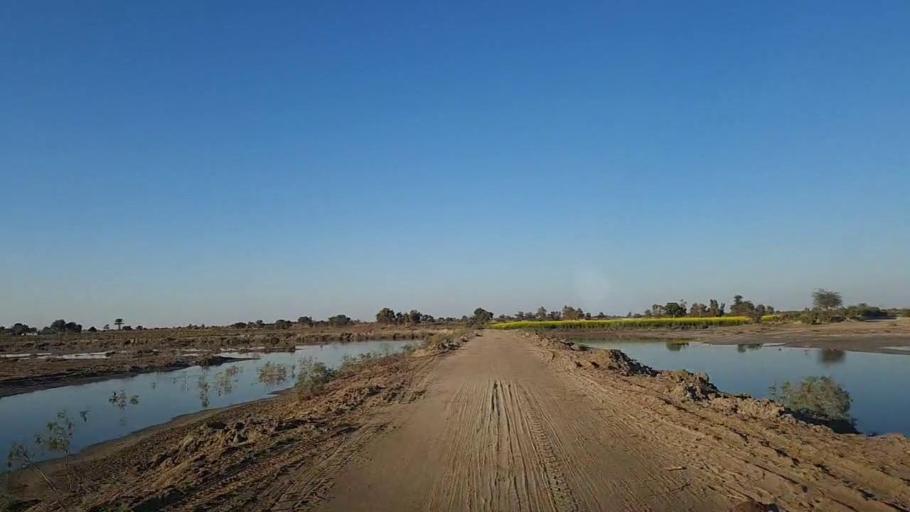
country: PK
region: Sindh
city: Sanghar
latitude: 26.1466
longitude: 68.9265
